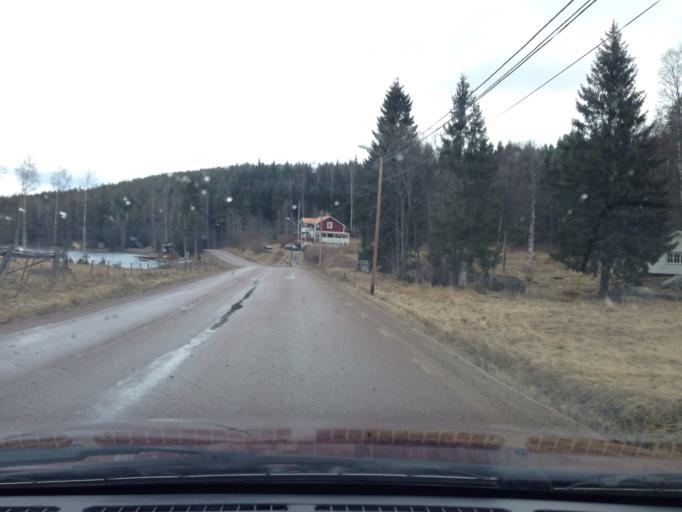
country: SE
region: Dalarna
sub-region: Ludvika Kommun
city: Ludvika
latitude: 60.1554
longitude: 15.2632
